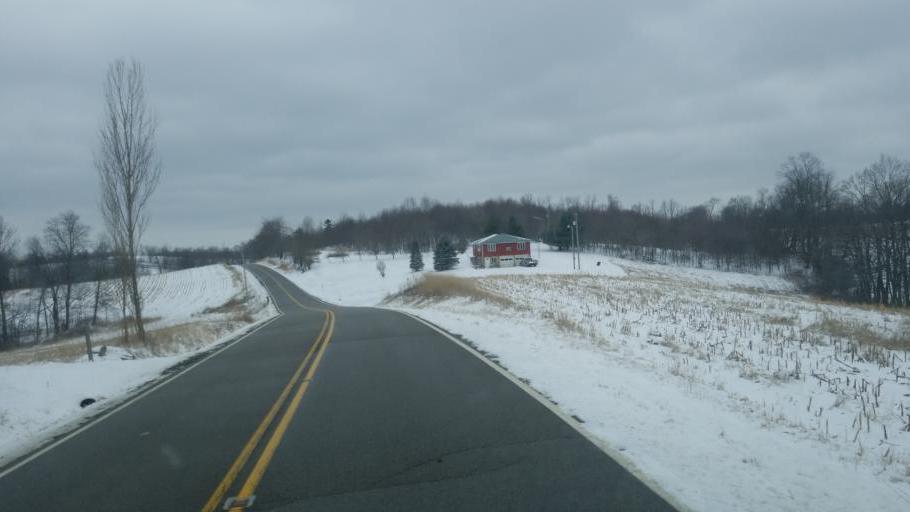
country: US
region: Ohio
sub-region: Knox County
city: Oak Hill
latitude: 40.3881
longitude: -82.1302
